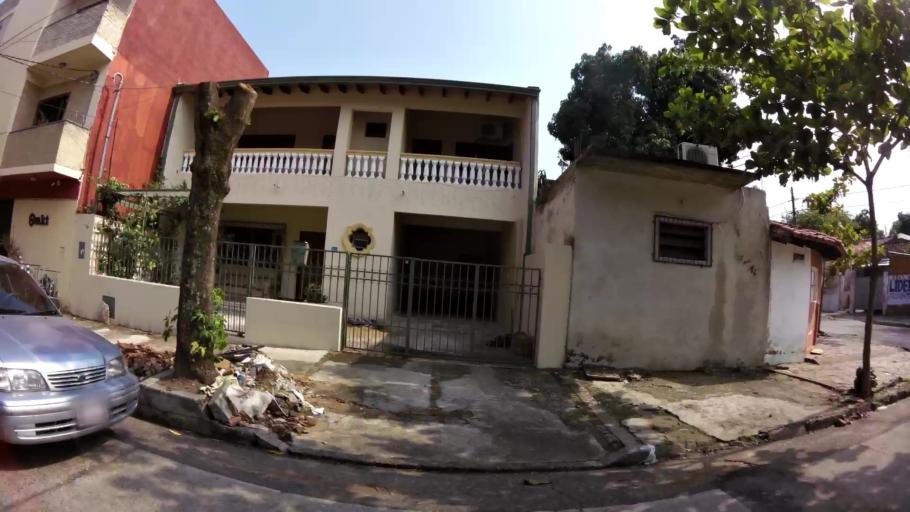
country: PY
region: Presidente Hayes
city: Nanawa
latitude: -25.2950
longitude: -57.6641
